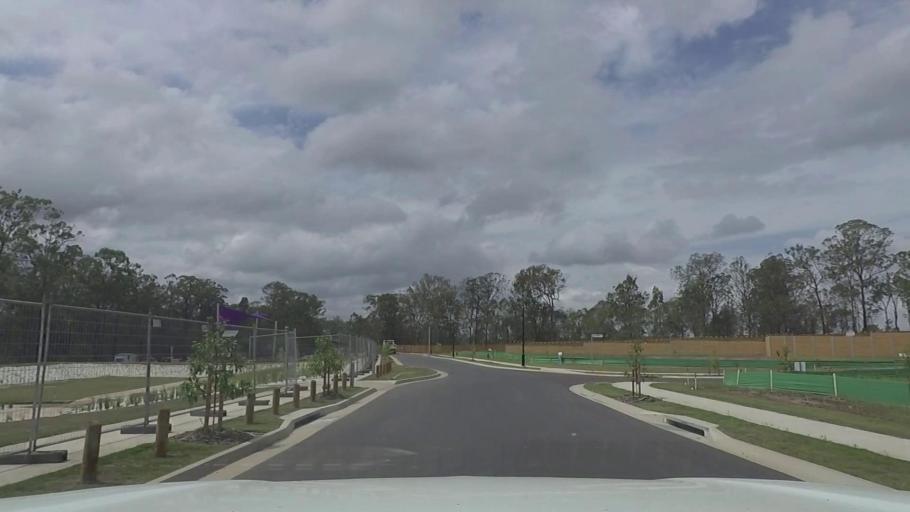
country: AU
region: Queensland
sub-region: Logan
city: Waterford West
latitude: -27.7016
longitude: 153.1074
